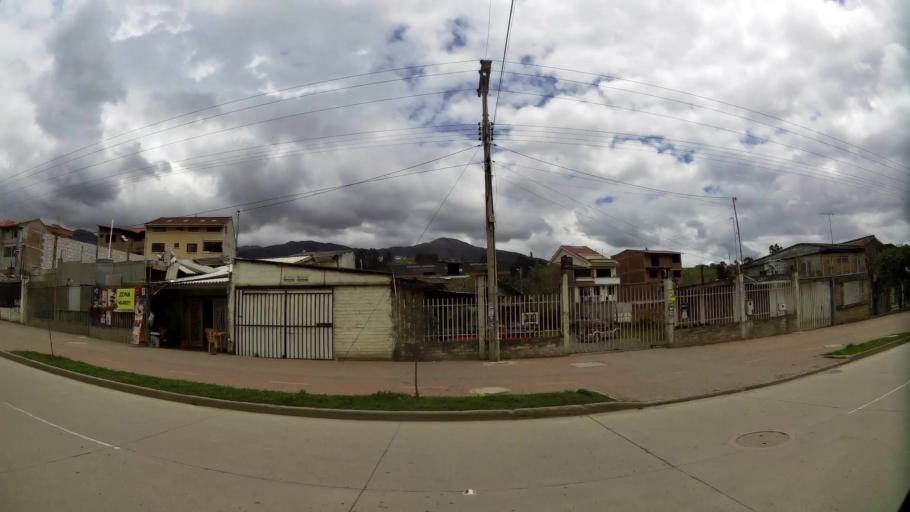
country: EC
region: Azuay
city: Cuenca
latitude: -2.8803
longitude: -79.0660
